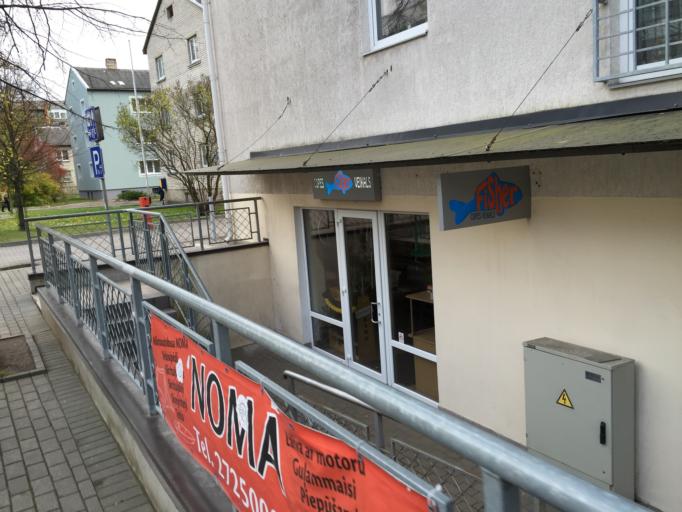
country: LV
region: Tukuma Rajons
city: Tukums
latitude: 56.9683
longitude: 23.1584
